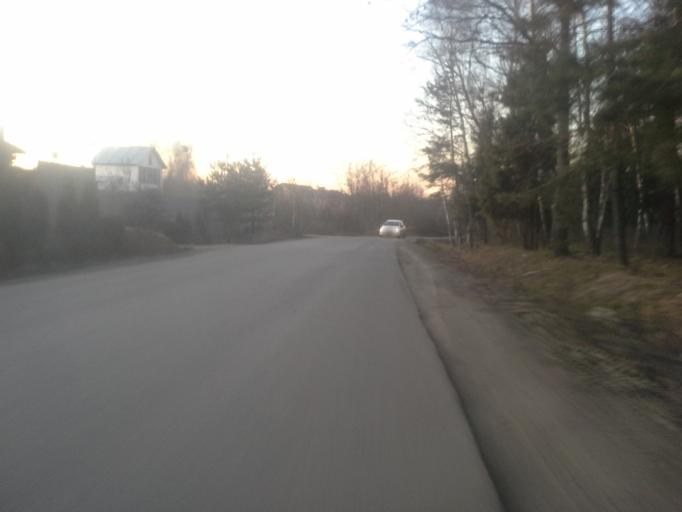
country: RU
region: Moscow
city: Tolstopal'tsevo
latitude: 55.6108
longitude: 37.2327
